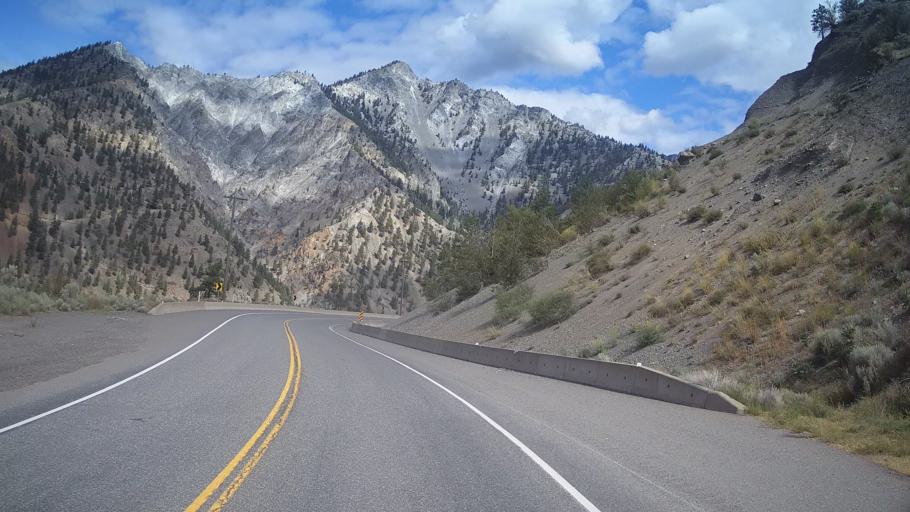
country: CA
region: British Columbia
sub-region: Thompson-Nicola Regional District
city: Ashcroft
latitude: 50.2532
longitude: -121.4741
